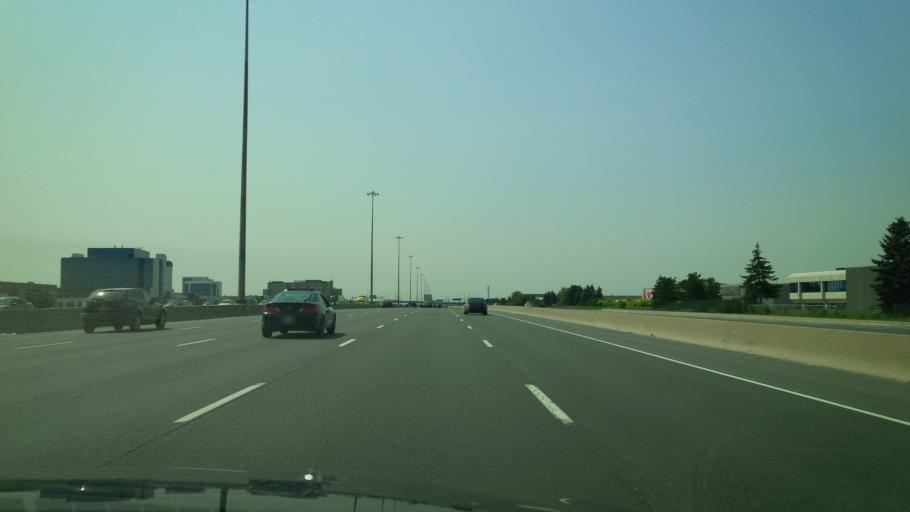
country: CA
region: Ontario
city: Vaughan
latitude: 43.8069
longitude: -79.5433
